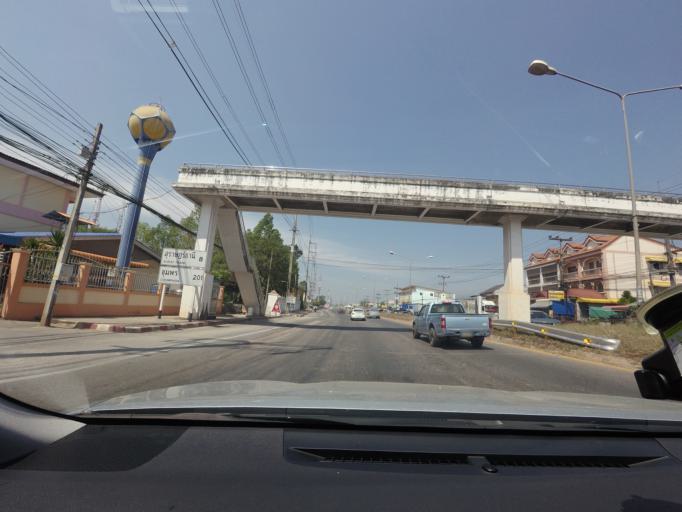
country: TH
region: Surat Thani
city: Surat Thani
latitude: 9.1484
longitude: 99.3912
